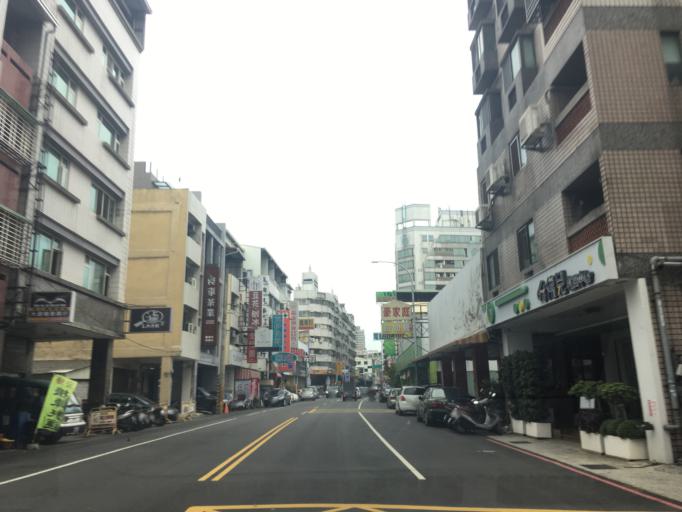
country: TW
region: Taiwan
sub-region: Taichung City
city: Taichung
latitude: 24.1756
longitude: 120.6892
